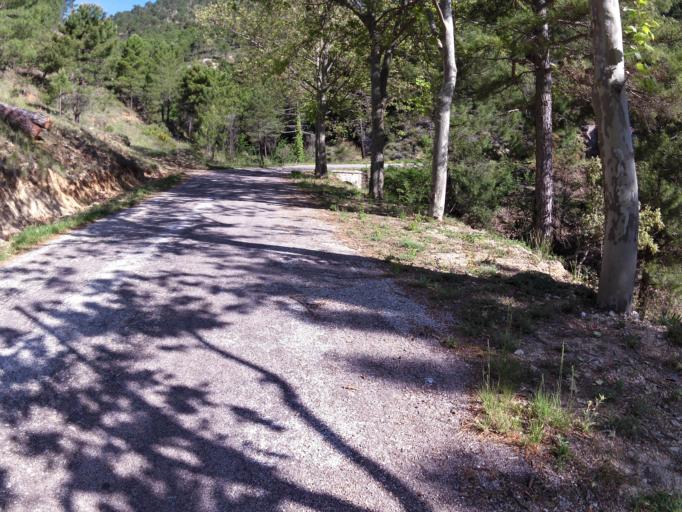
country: ES
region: Castille-La Mancha
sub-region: Provincia de Albacete
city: Riopar
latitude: 38.5237
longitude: -2.4560
